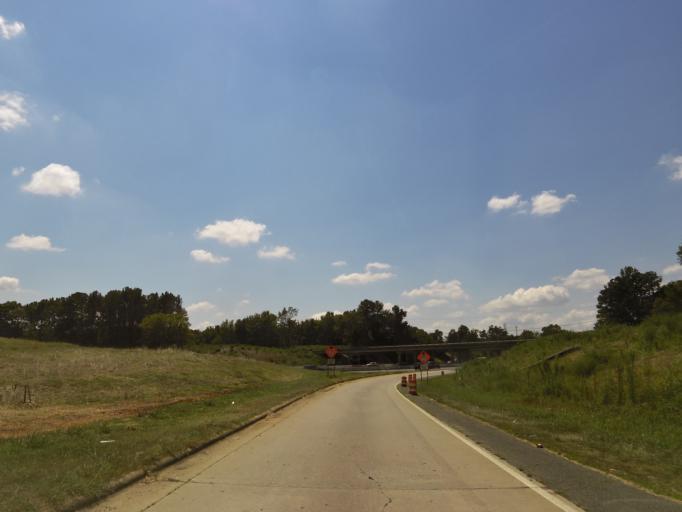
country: US
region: North Carolina
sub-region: Cabarrus County
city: Kannapolis
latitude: 35.4466
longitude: -80.6108
